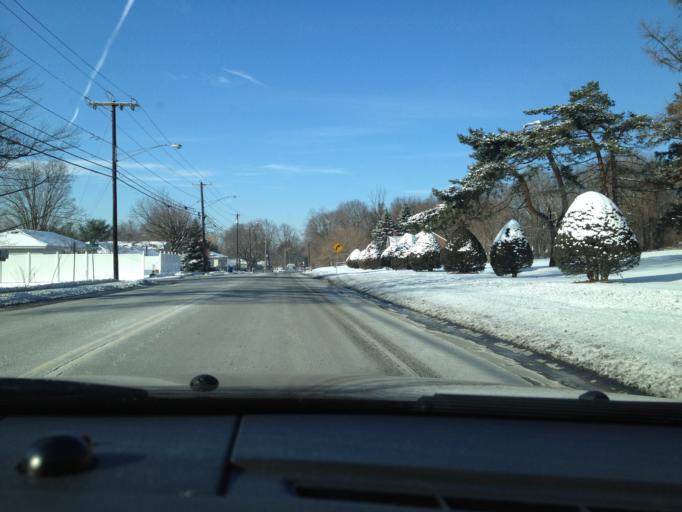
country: US
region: New York
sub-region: Albany County
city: West Albany
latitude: 42.6994
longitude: -73.7713
